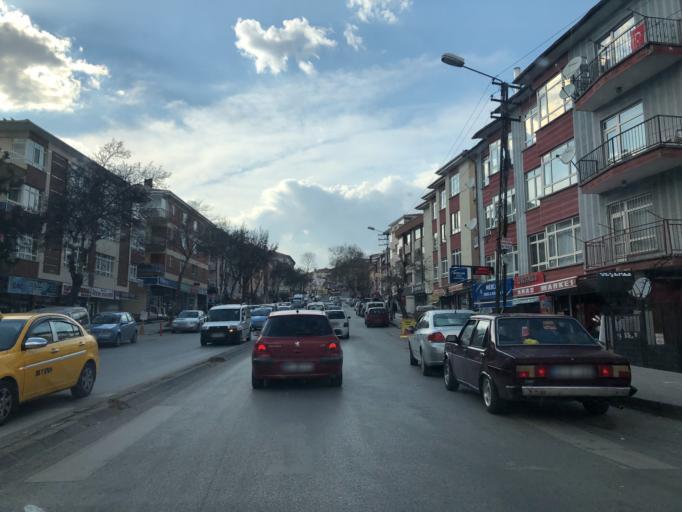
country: TR
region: Ankara
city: Ankara
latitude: 39.9845
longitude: 32.8570
